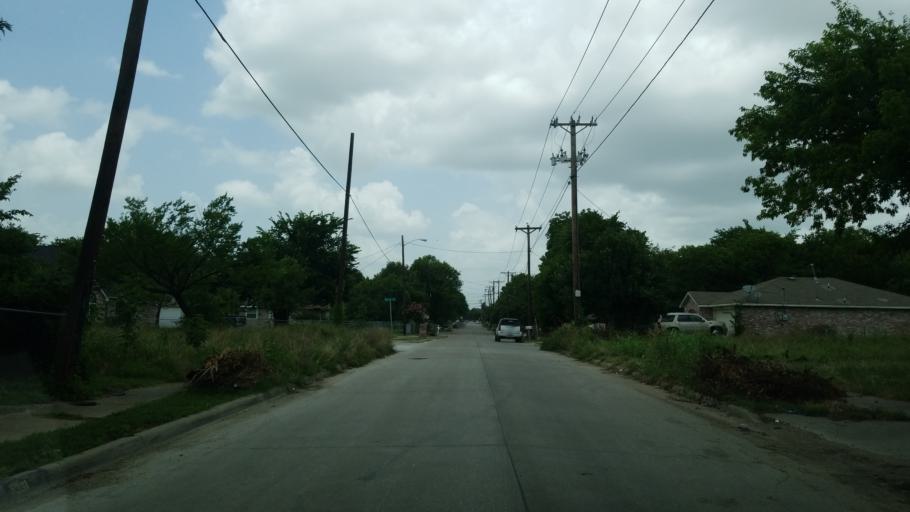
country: US
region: Texas
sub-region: Dallas County
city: Cockrell Hill
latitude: 32.7832
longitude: -96.8971
